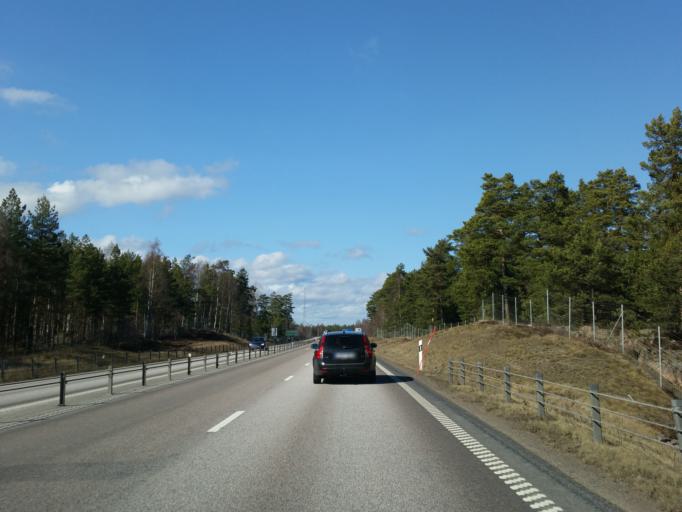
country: SE
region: Kalmar
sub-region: Oskarshamns Kommun
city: Oskarshamn
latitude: 57.2428
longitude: 16.4304
